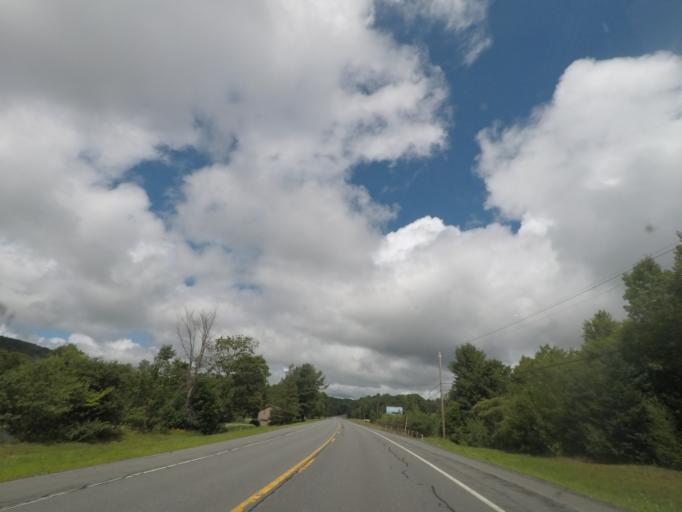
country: US
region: Massachusetts
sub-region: Berkshire County
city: Lanesborough
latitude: 42.5662
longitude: -73.3685
